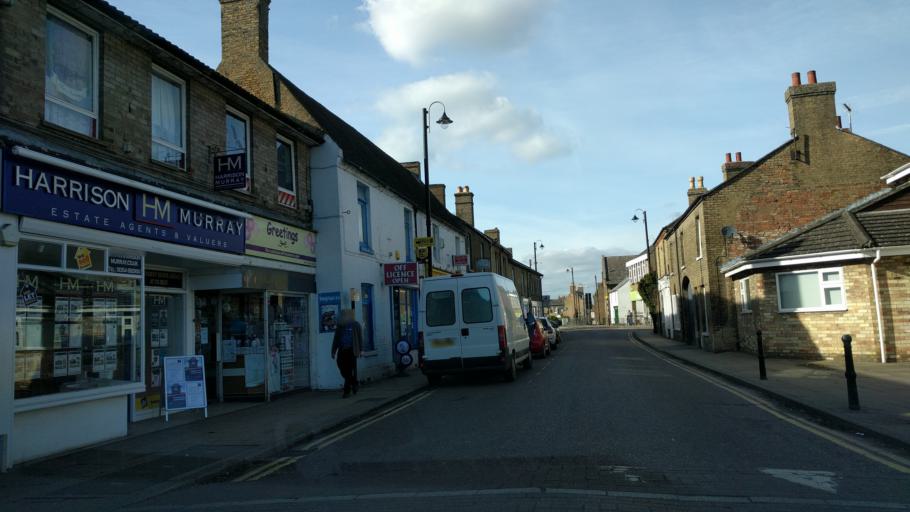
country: GB
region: England
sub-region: Cambridgeshire
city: Chatteris
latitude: 52.4565
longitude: 0.0486
